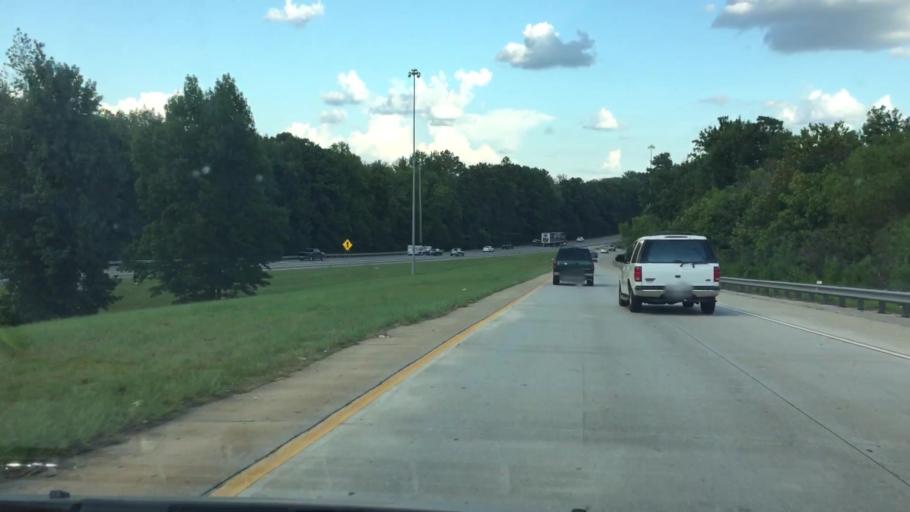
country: US
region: Georgia
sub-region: Henry County
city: Stockbridge
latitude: 33.5032
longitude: -84.2298
